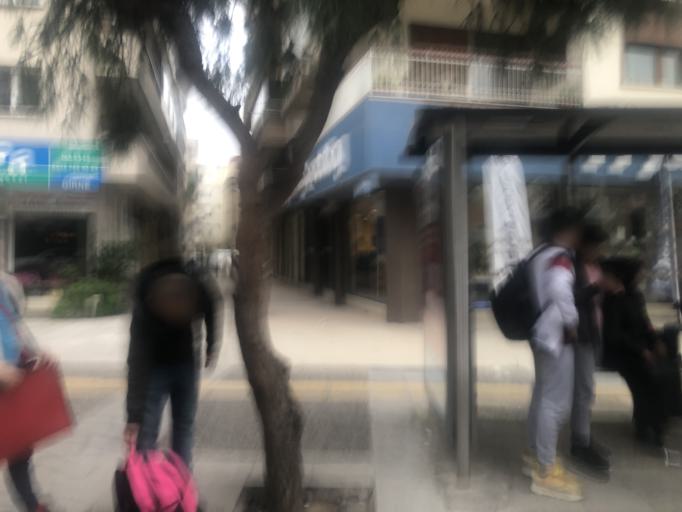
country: TR
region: Izmir
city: Karsiyaka
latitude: 38.4544
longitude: 27.1065
